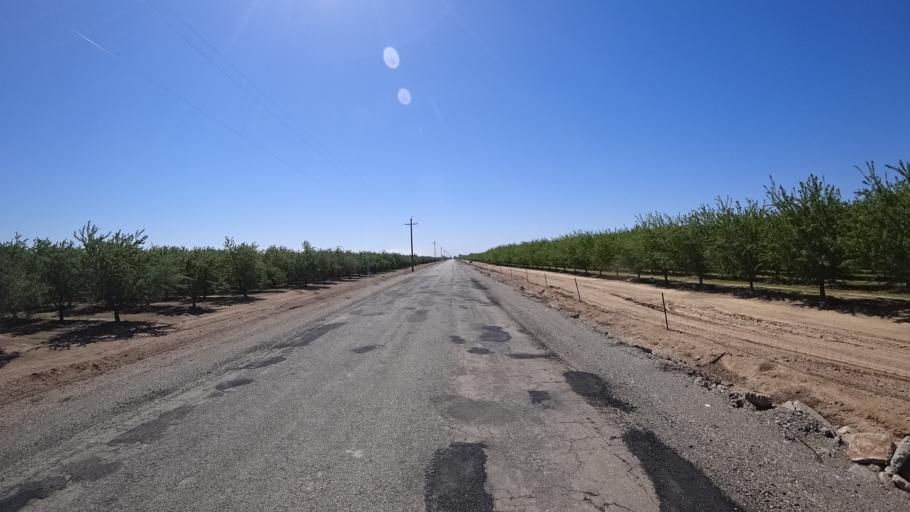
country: US
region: California
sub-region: Glenn County
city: Orland
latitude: 39.6440
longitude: -122.2346
